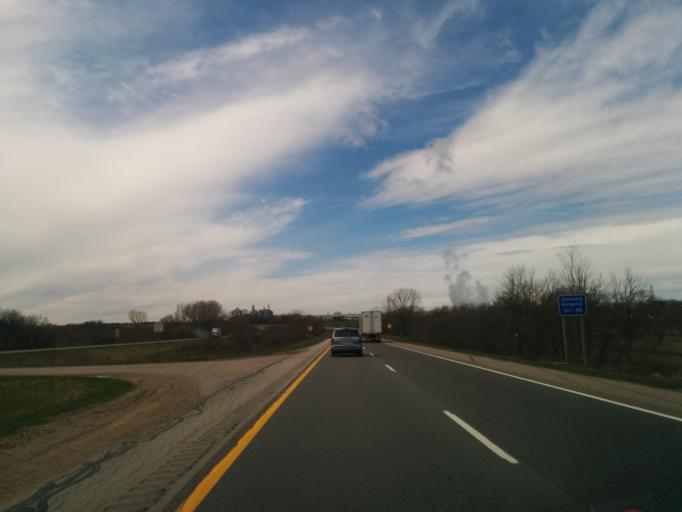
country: US
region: Michigan
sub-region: Ottawa County
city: Zeeland
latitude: 42.8177
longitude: -85.9646
